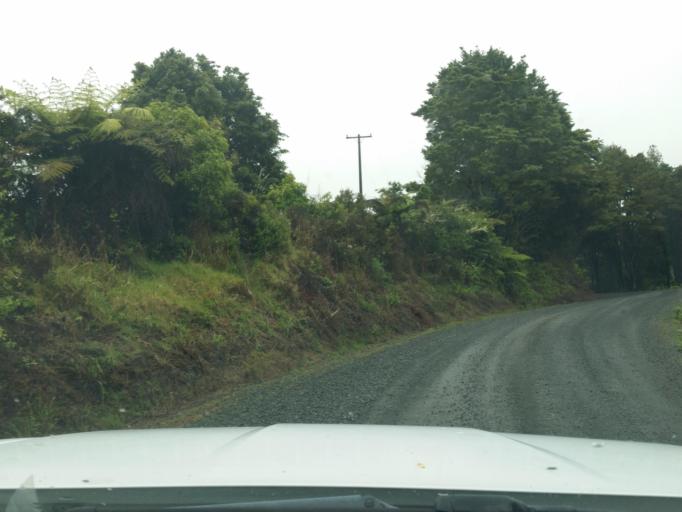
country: NZ
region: Northland
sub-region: Kaipara District
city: Dargaville
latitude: -35.7587
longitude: 173.9275
